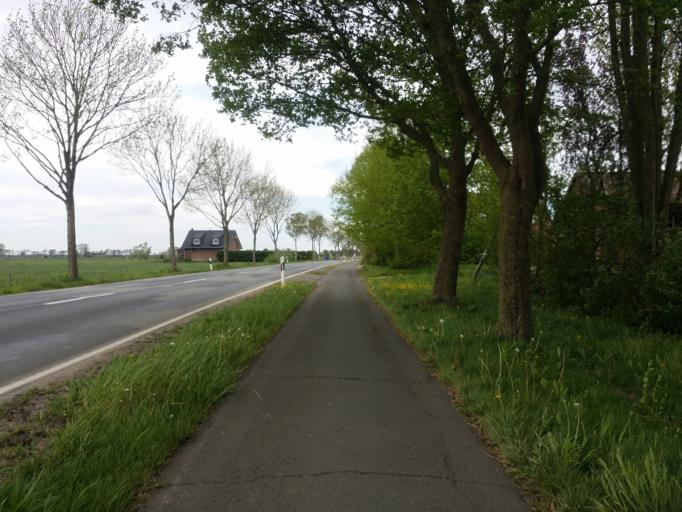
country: DE
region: Lower Saxony
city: Lemwerder
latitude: 53.1433
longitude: 8.5635
